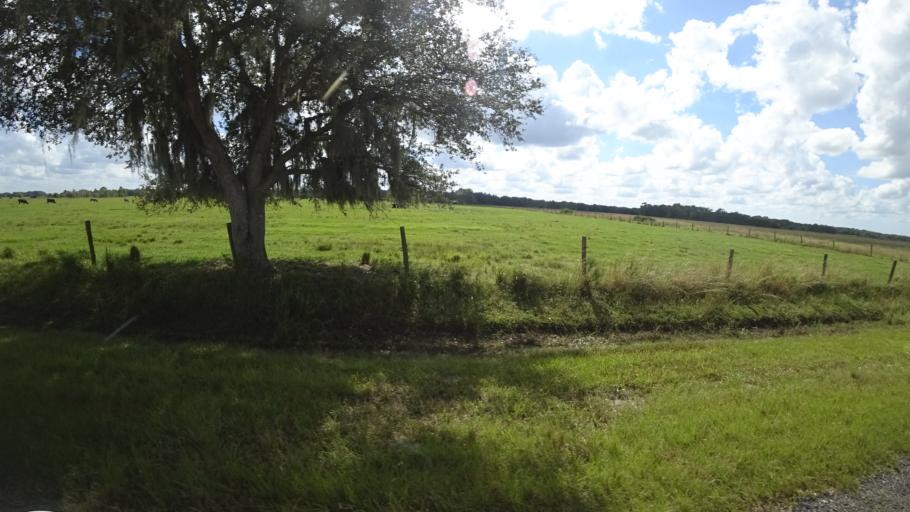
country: US
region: Florida
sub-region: Sarasota County
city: Warm Mineral Springs
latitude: 27.2739
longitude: -82.1951
